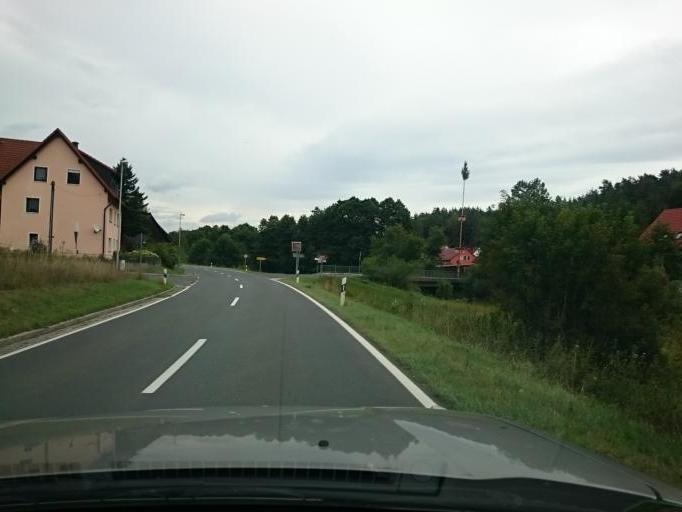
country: DE
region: Bavaria
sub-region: Regierungsbezirk Mittelfranken
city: Neuhaus an der Pegnitz
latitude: 49.6143
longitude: 11.5401
